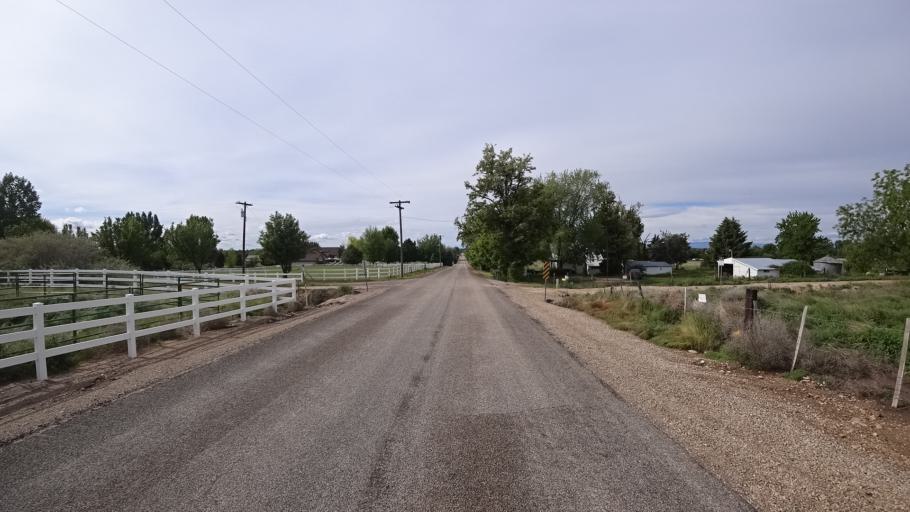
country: US
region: Idaho
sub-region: Ada County
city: Eagle
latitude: 43.7340
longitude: -116.4034
